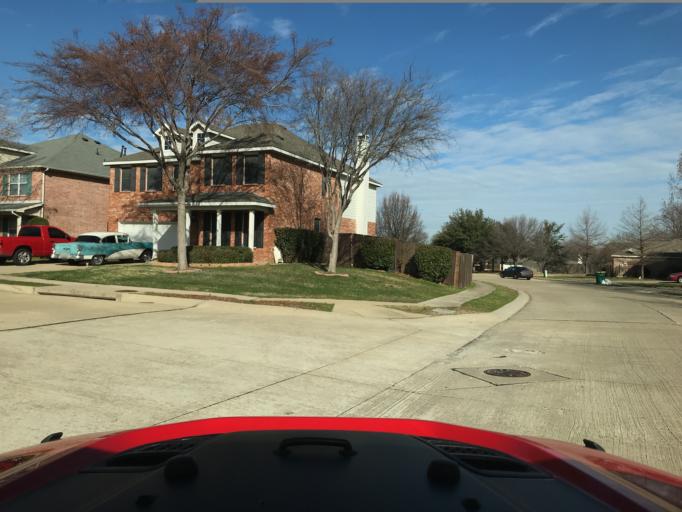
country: US
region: Texas
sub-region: Denton County
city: Lewisville
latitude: 33.0477
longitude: -97.0321
